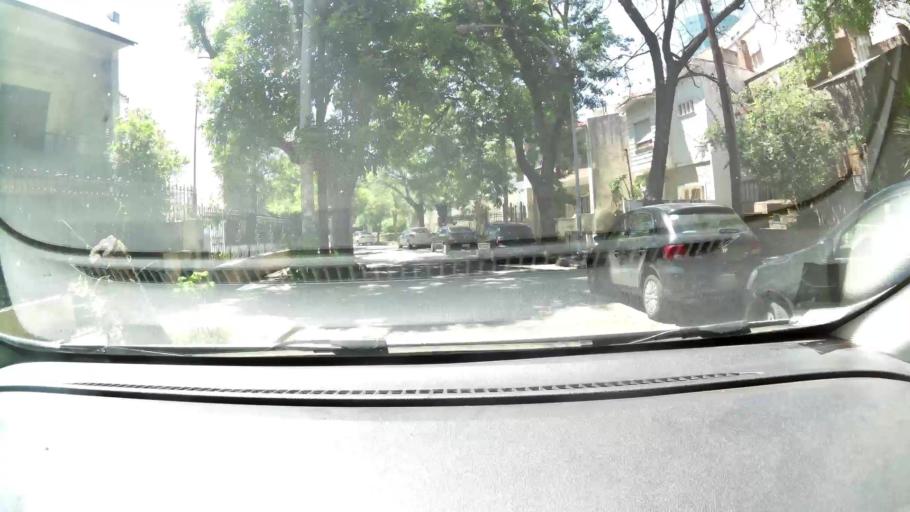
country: AR
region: Cordoba
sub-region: Departamento de Capital
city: Cordoba
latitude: -31.4121
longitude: -64.2038
